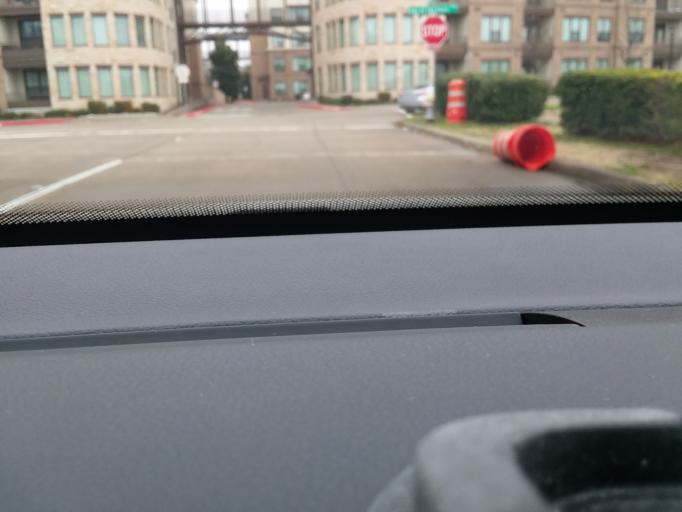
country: US
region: Texas
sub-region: Collin County
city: Frisco
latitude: 33.0974
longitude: -96.8193
